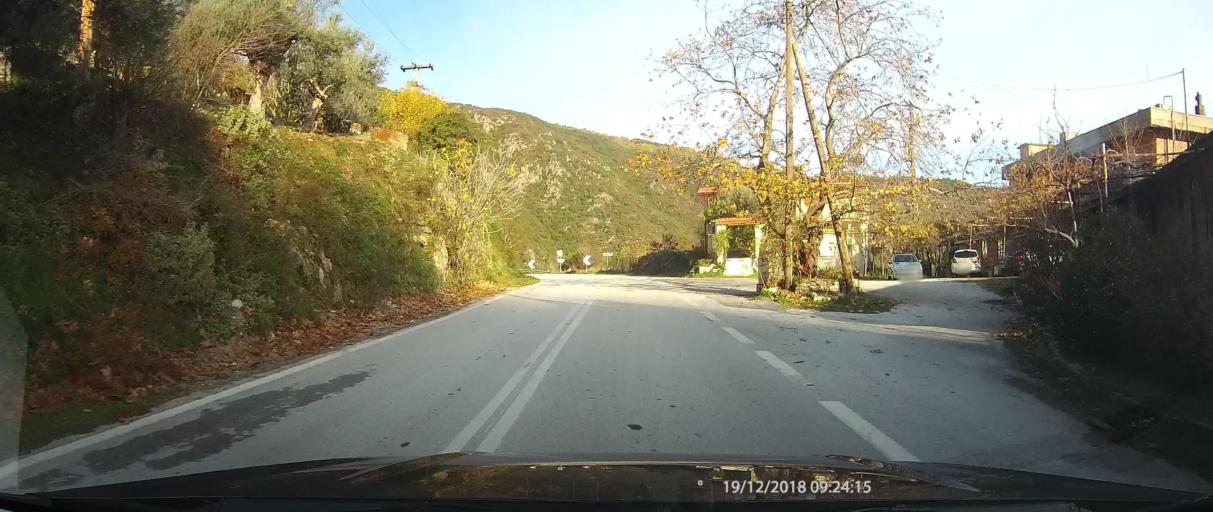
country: GR
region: Peloponnese
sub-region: Nomos Lakonias
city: Magoula
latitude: 37.0955
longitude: 22.3413
